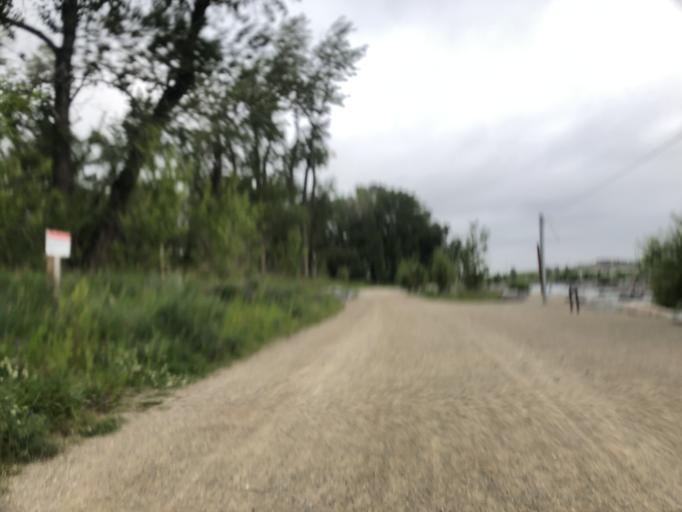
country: CA
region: Alberta
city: Calgary
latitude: 51.0413
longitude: -114.0125
